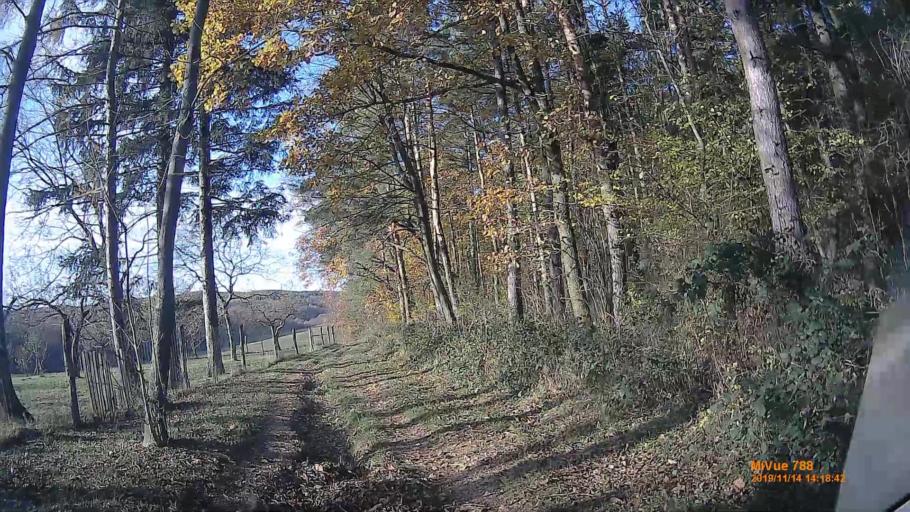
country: HU
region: Veszprem
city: Herend
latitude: 47.2062
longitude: 17.7798
